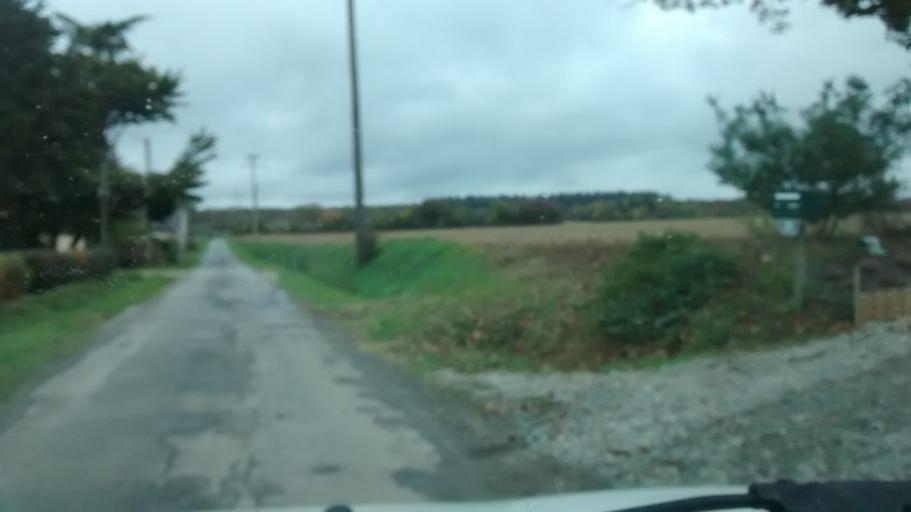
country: FR
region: Brittany
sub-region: Departement d'Ille-et-Vilaine
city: Servon-sur-Vilaine
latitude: 48.1299
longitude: -1.4435
